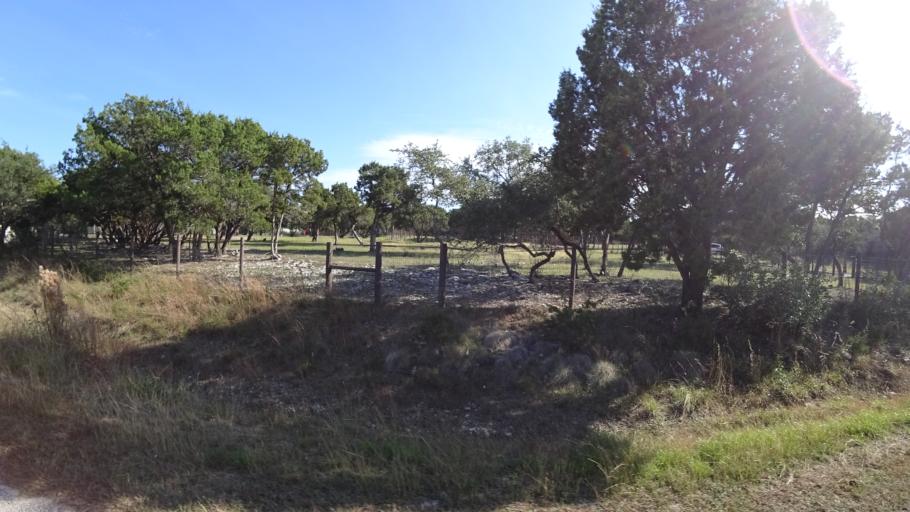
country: US
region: Texas
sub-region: Travis County
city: Bee Cave
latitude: 30.2364
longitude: -97.9406
